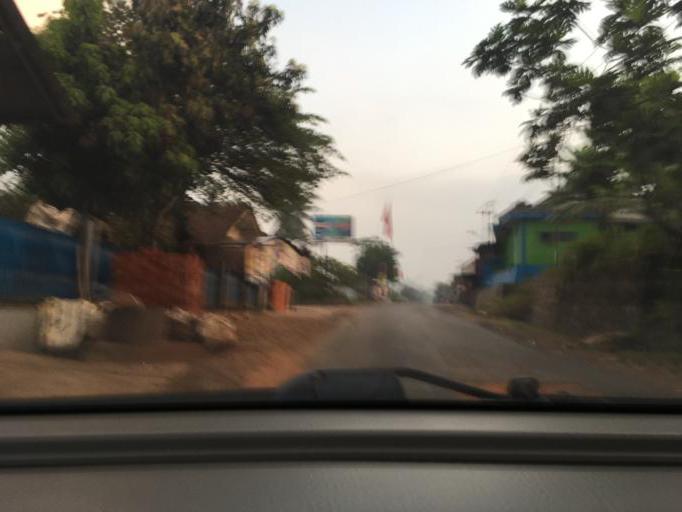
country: ID
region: West Java
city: Pasireurih
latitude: -7.1858
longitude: 108.1970
